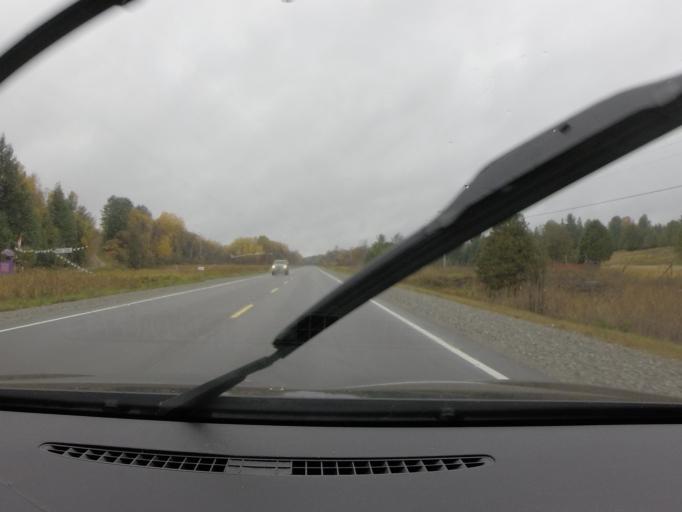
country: CA
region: Ontario
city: Skatepark
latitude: 44.7289
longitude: -76.9609
